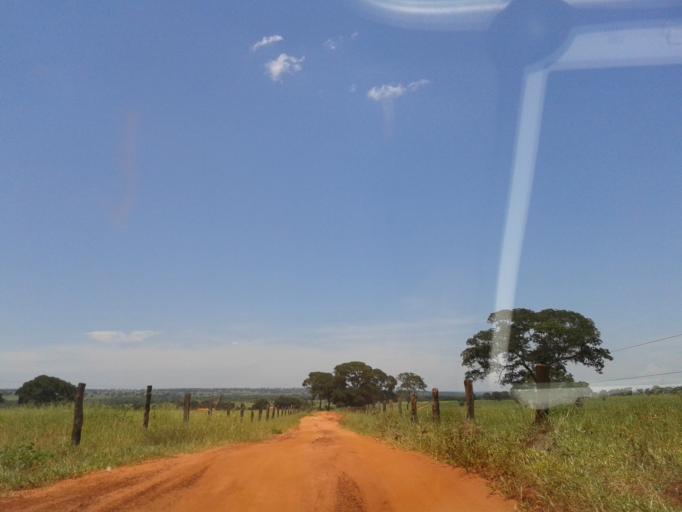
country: BR
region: Minas Gerais
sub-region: Santa Vitoria
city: Santa Vitoria
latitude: -19.2061
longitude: -50.3960
